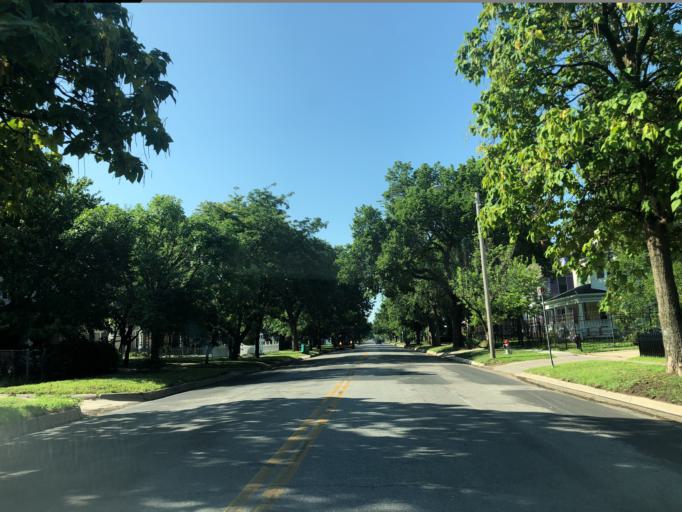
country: US
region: Kansas
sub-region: Sedgwick County
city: Wichita
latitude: 37.7064
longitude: -97.3420
